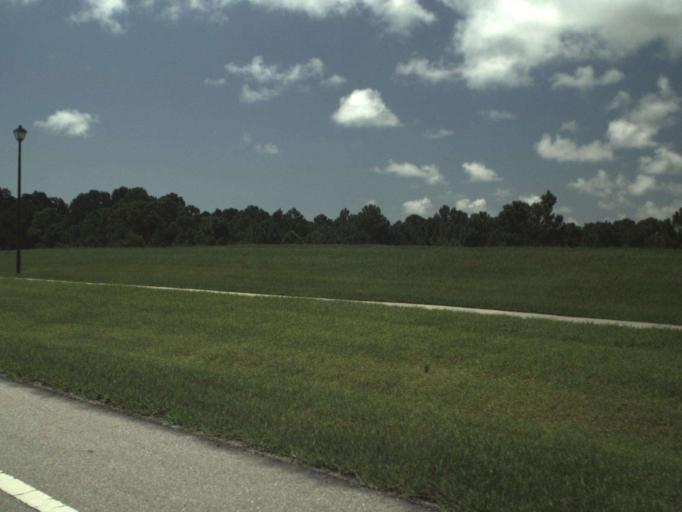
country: US
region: Florida
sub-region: Indian River County
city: Gifford
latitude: 27.6899
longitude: -80.4235
